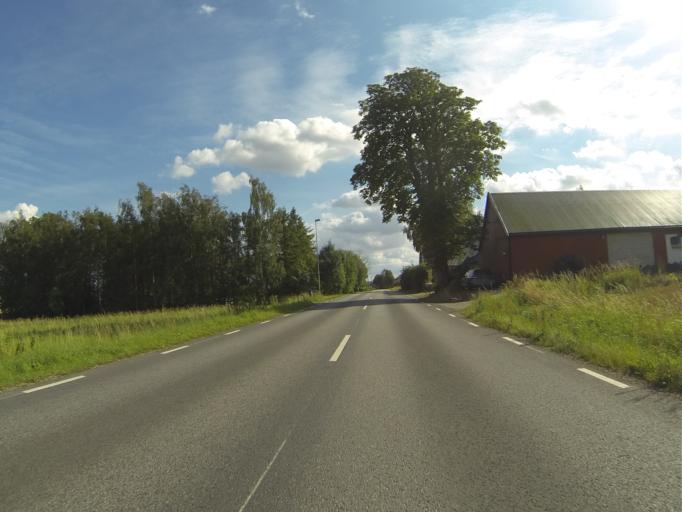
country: SE
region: Skane
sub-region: Eslovs Kommun
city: Eslov
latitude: 55.7369
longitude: 13.3315
